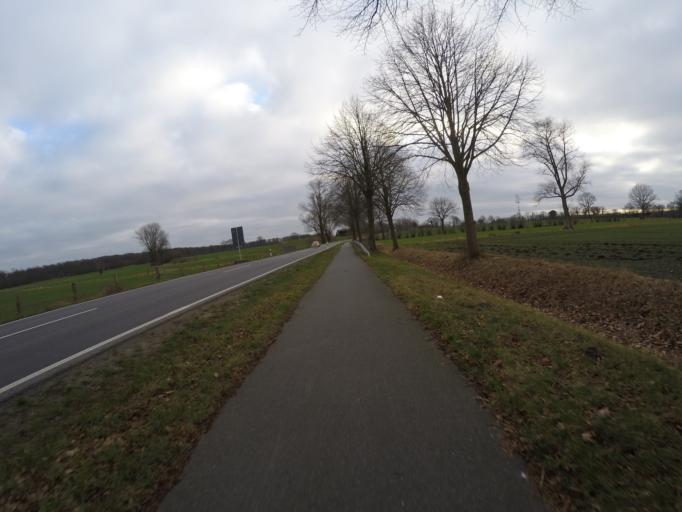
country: DE
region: Schleswig-Holstein
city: Alveslohe
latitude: 53.7824
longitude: 9.9088
